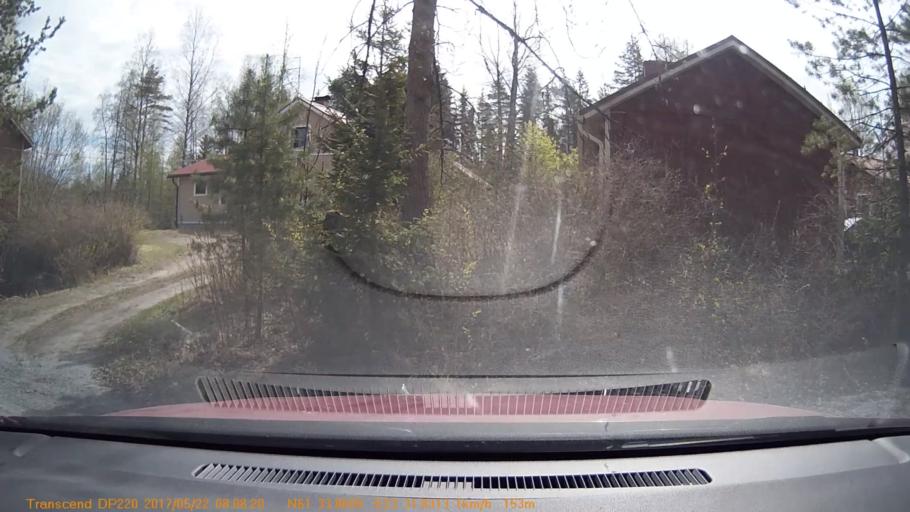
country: FI
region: Pirkanmaa
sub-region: Tampere
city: Yloejaervi
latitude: 61.5644
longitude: 23.5306
